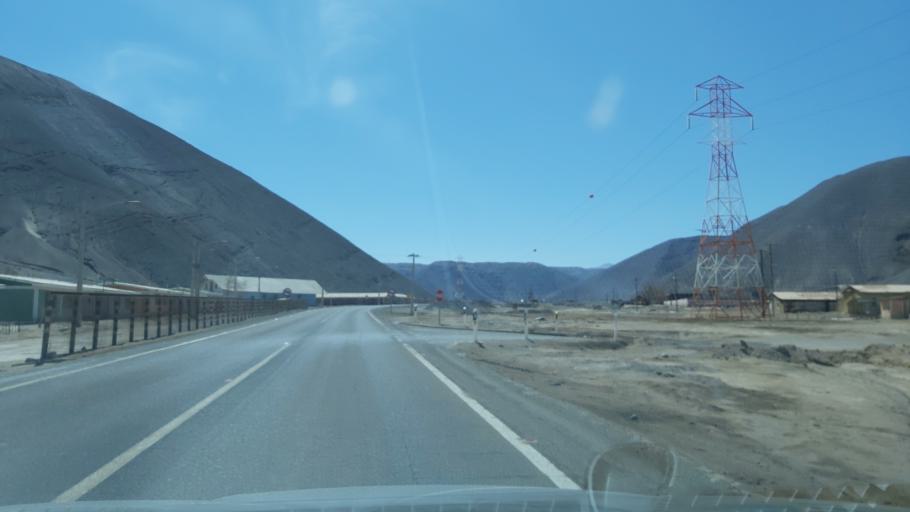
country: CL
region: Atacama
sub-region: Provincia de Chanaral
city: Diego de Almagro
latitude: -26.3326
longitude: -69.8220
